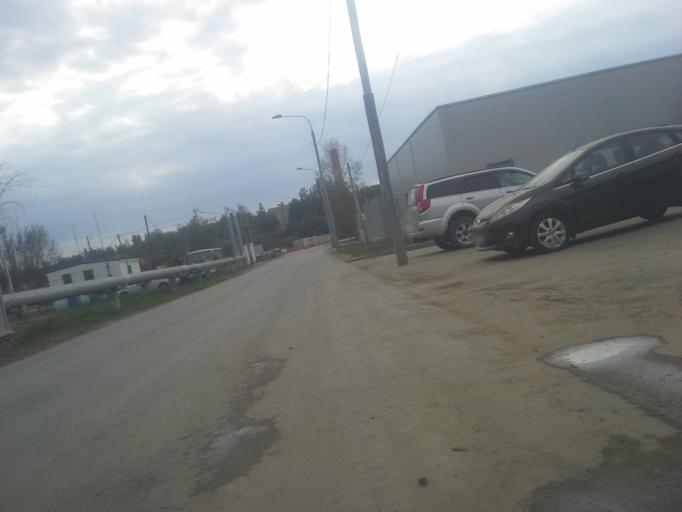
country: RU
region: Moskovskaya
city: Kievskij
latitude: 55.4275
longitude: 36.8690
